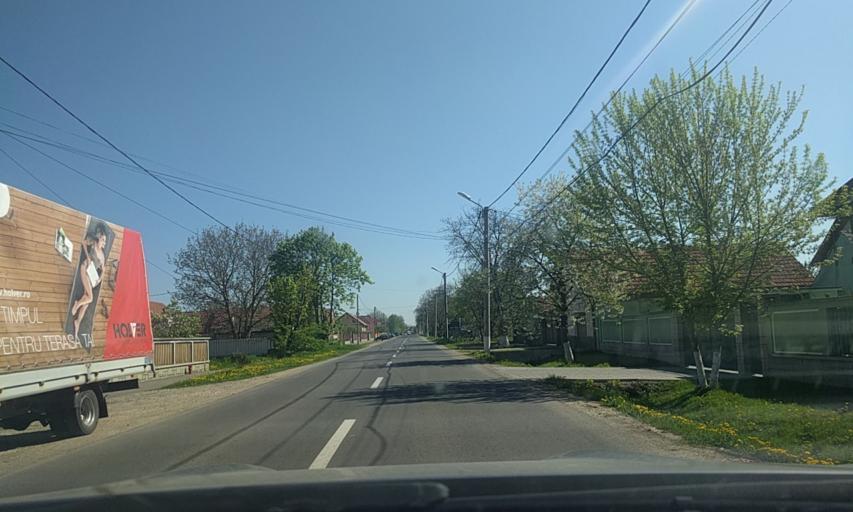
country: RO
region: Brasov
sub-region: Comuna Bod
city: Colonia Bod
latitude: 45.7015
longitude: 25.5648
